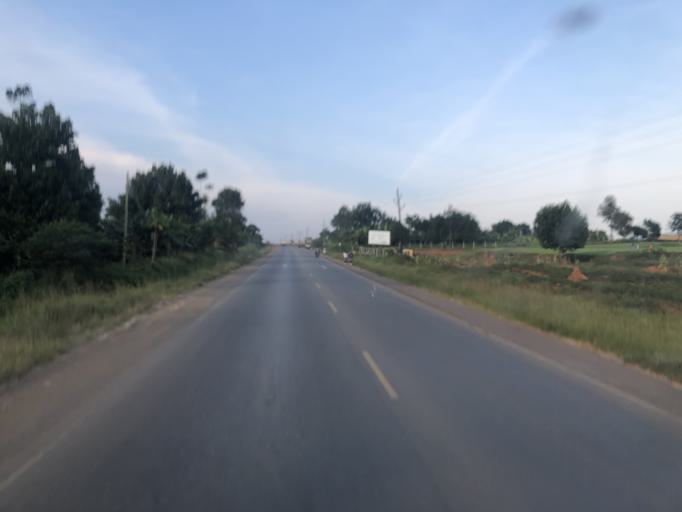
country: UG
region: Central Region
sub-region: Mpigi District
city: Mpigi
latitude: 0.2044
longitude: 32.3103
